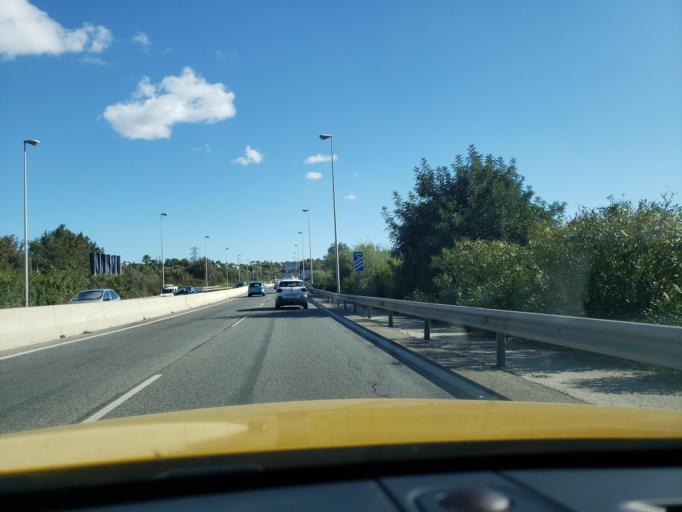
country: ES
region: Andalusia
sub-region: Provincia de Malaga
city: Marbella
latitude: 36.5059
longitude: -4.8192
